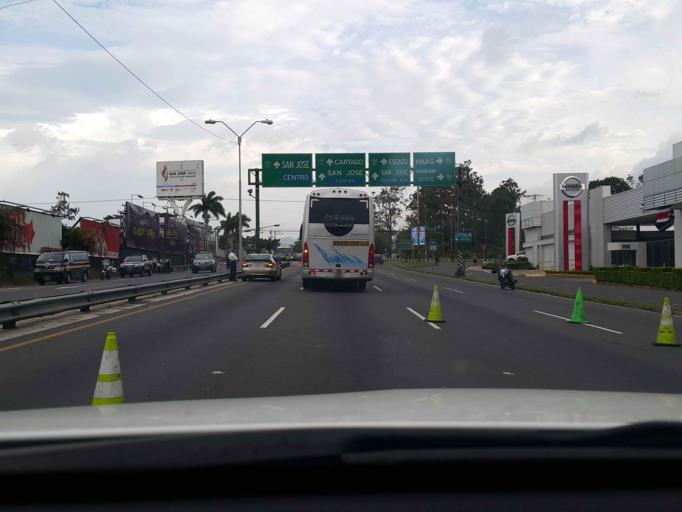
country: CR
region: San Jose
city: San Jose
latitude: 9.9392
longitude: -84.0984
